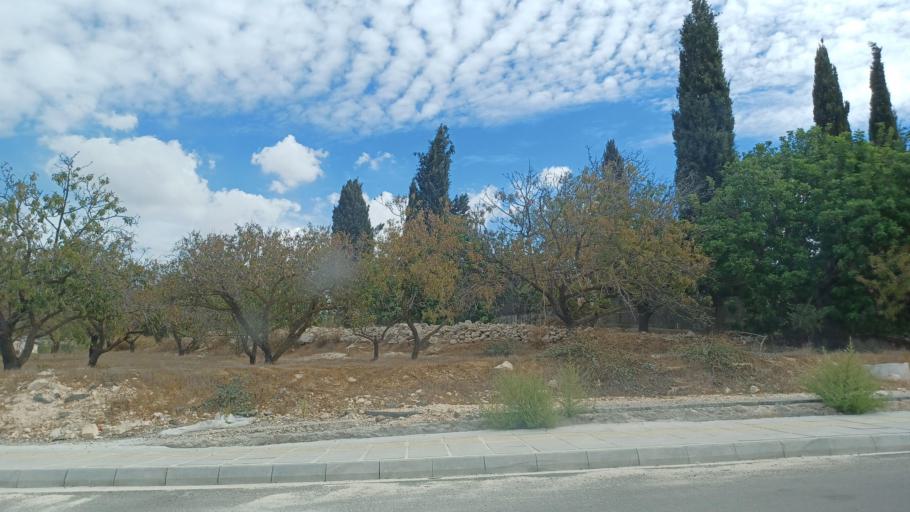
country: CY
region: Pafos
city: Mesogi
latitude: 34.8188
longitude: 32.4592
